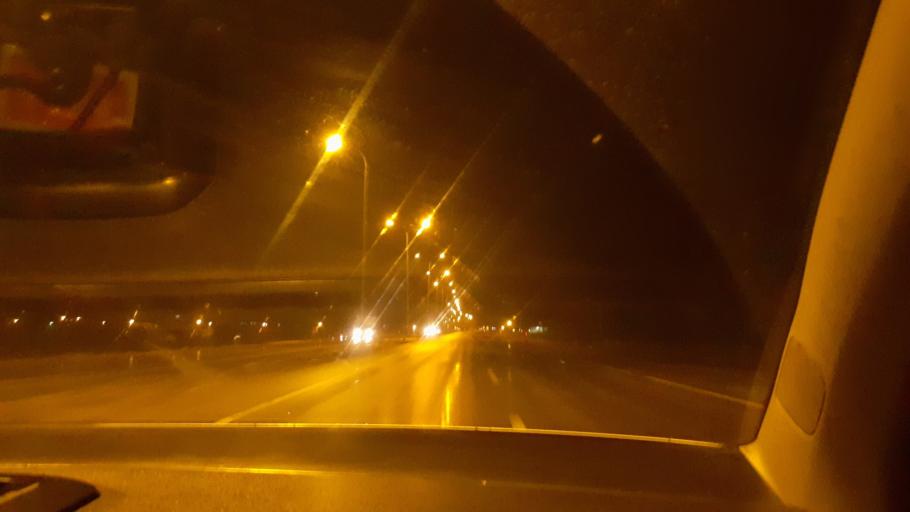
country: TR
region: Hatay
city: Aktepe
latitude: 36.7183
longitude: 36.5120
